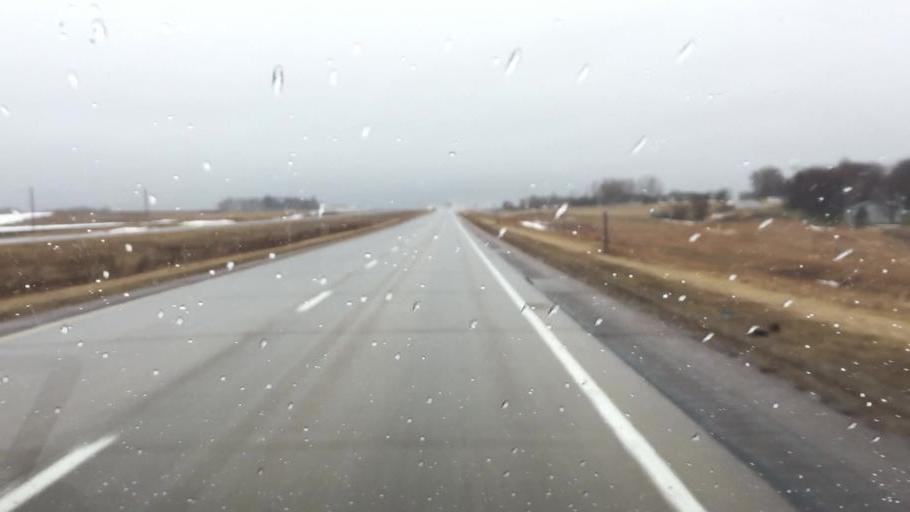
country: US
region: Iowa
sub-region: O'Brien County
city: Sheldon
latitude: 43.0782
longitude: -95.8995
